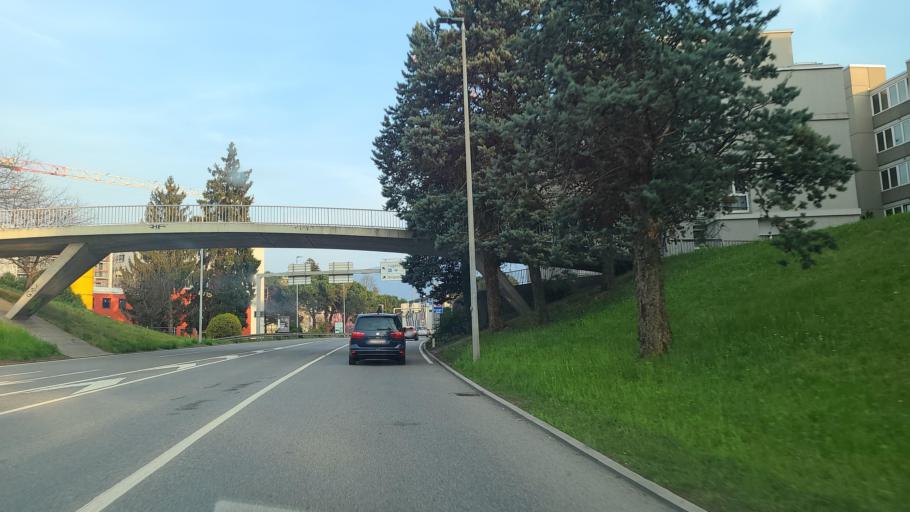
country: CH
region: Ticino
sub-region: Lugano District
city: Massagno
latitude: 46.0155
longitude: 8.9393
